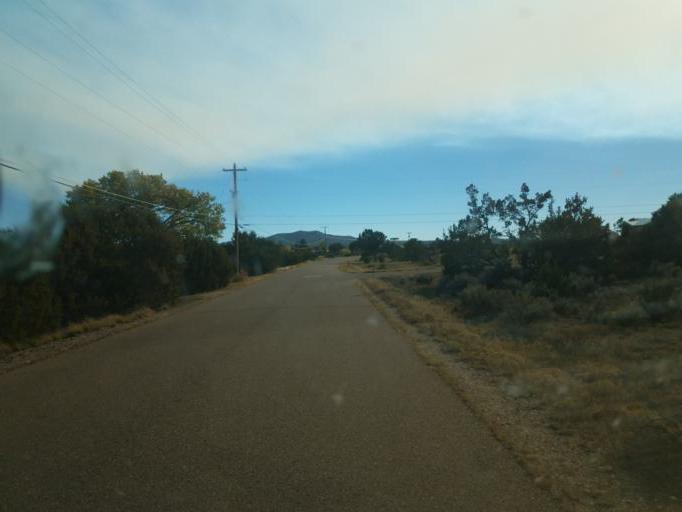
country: US
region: New Mexico
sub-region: Los Alamos County
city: White Rock
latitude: 35.8068
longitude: -106.2136
